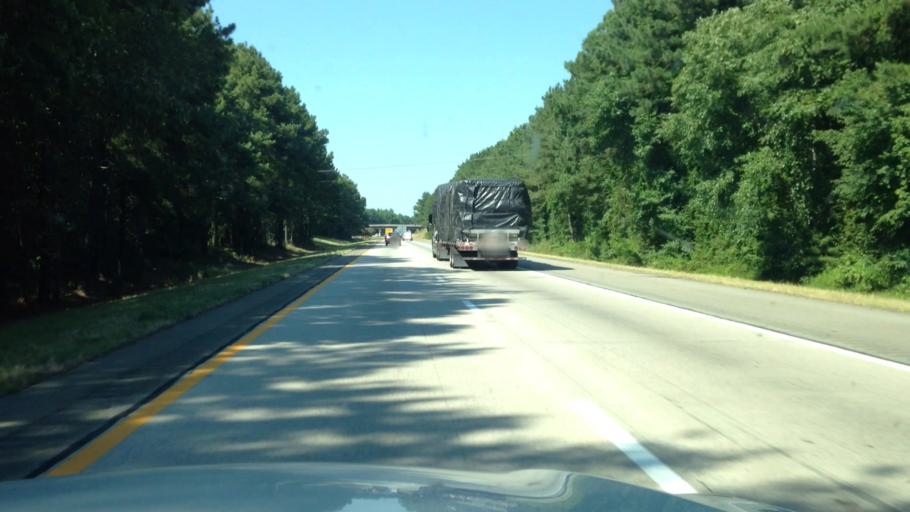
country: US
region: North Carolina
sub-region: Nash County
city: Nashville
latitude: 35.9146
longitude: -77.9186
